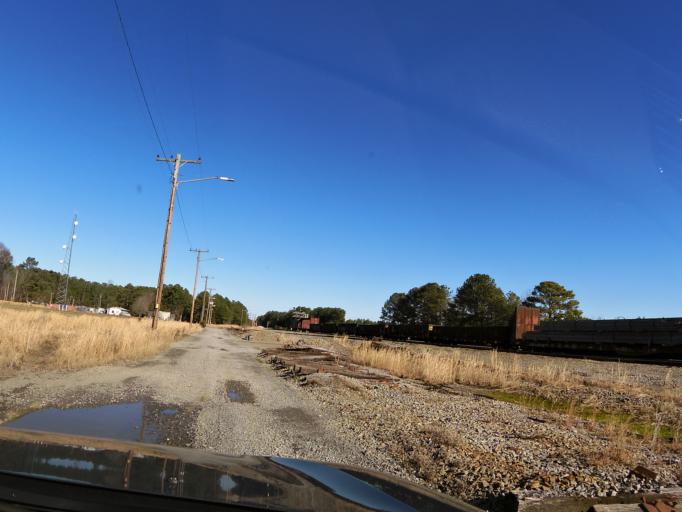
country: US
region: Virginia
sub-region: City of Petersburg
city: Petersburg
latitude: 37.1780
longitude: -77.4211
